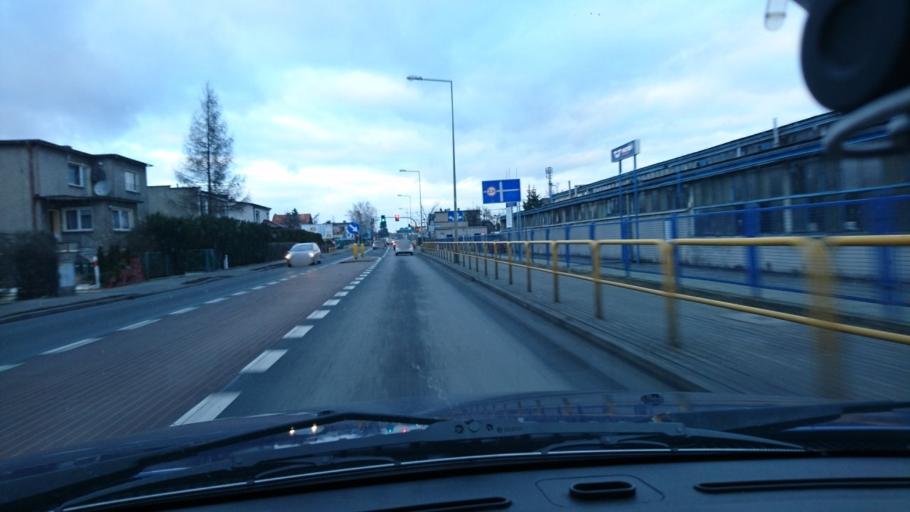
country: PL
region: Greater Poland Voivodeship
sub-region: Powiat kepinski
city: Kepno
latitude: 51.2768
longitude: 17.9904
